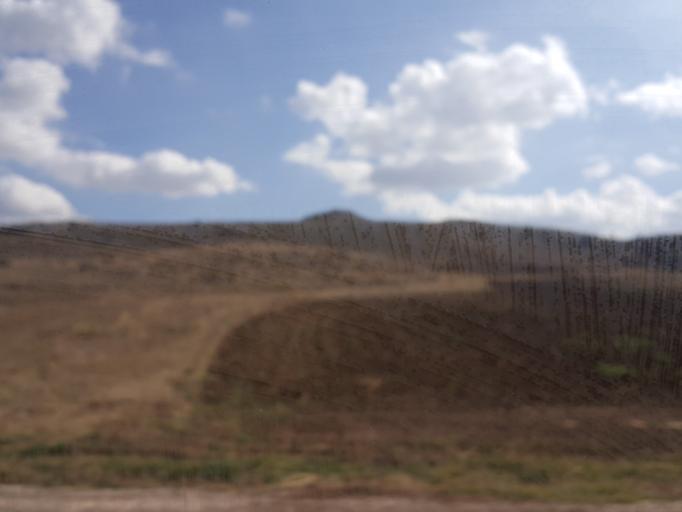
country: TR
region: Tokat
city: Artova
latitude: 40.1408
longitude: 36.3650
